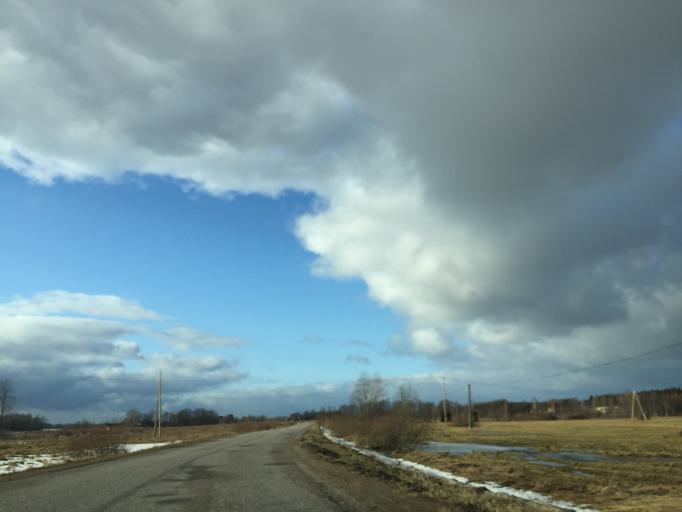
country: LV
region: Limbazu Rajons
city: Limbazi
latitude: 57.6087
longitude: 24.6048
